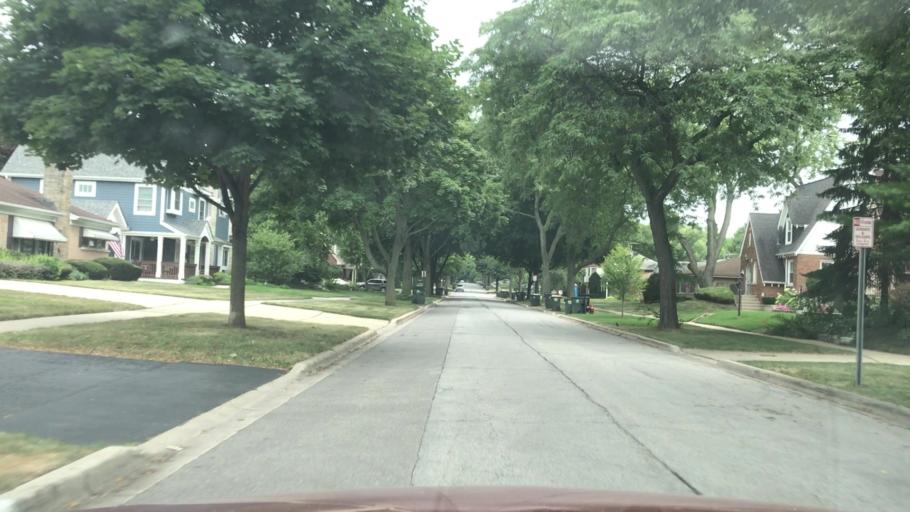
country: US
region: Illinois
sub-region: Cook County
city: Arlington Heights
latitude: 42.0754
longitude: -87.9879
